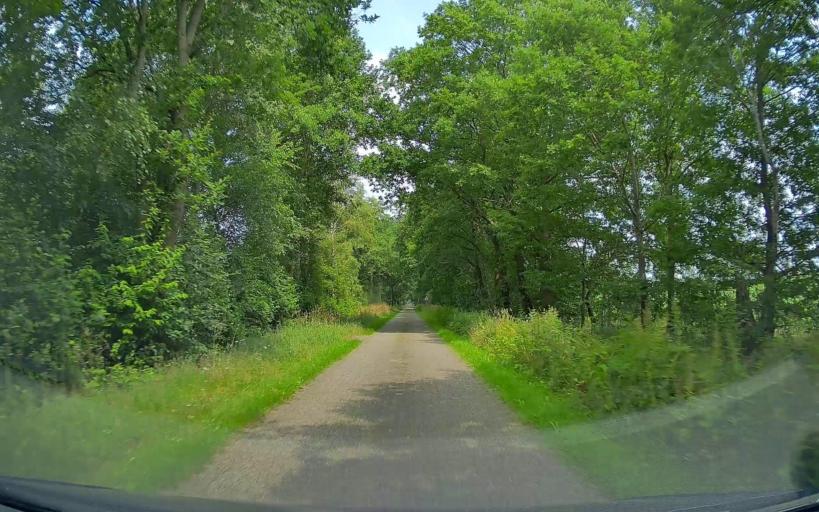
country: DE
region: Lower Saxony
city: Bosel
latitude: 53.0002
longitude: 7.9034
